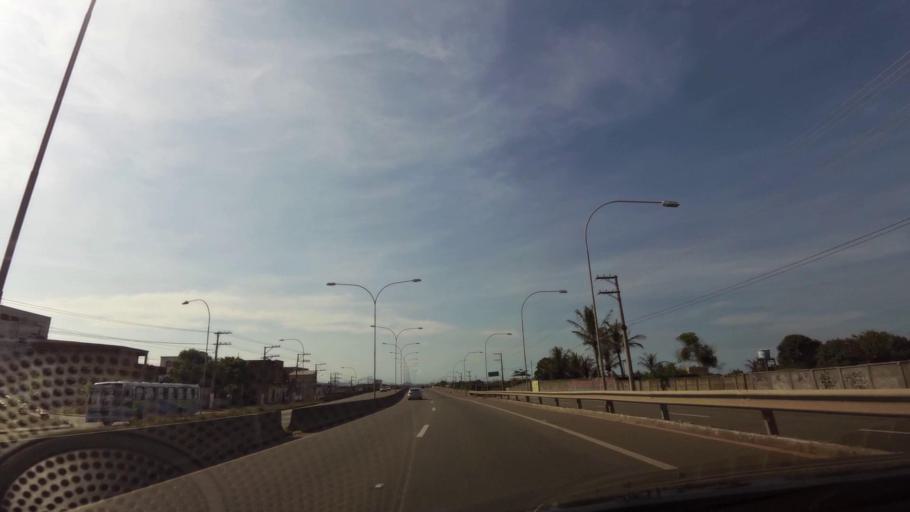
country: BR
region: Espirito Santo
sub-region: Vila Velha
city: Vila Velha
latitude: -20.4497
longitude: -40.3343
